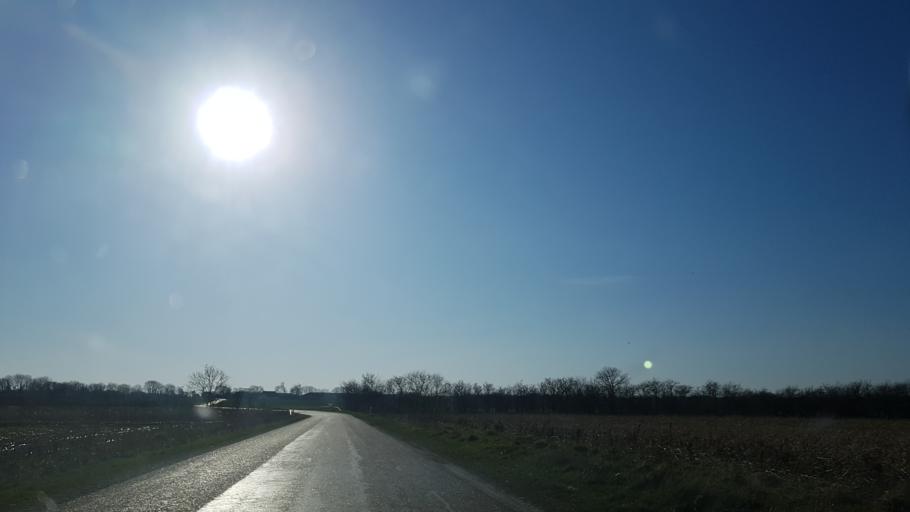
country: DK
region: South Denmark
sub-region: Vejen Kommune
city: Rodding
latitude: 55.3929
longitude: 9.0700
